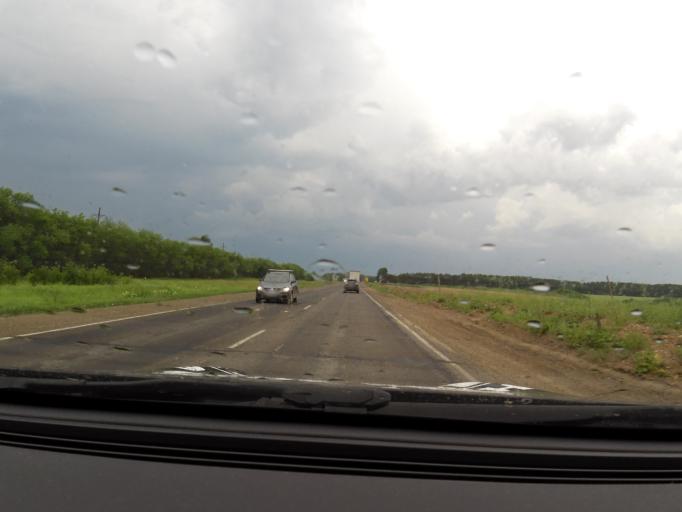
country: RU
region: Bashkortostan
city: Asanovo
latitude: 54.9153
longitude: 55.5901
